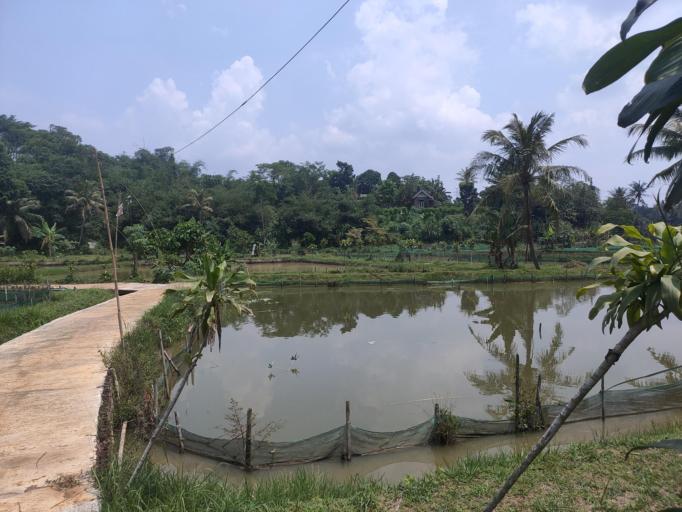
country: ID
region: West Java
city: Parung
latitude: -6.4688
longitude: 106.7105
